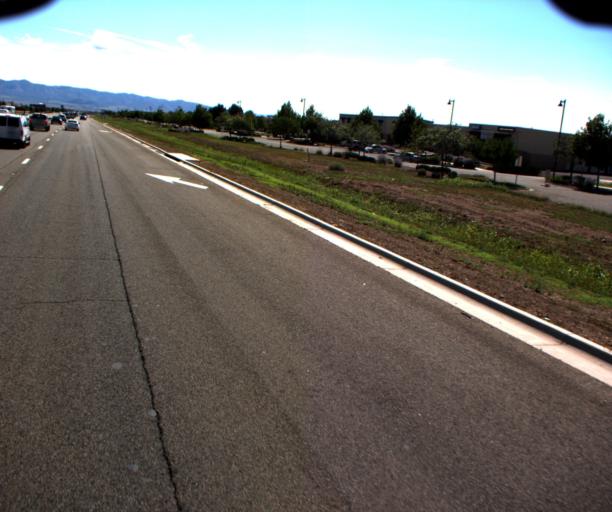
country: US
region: Arizona
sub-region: Yavapai County
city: Prescott Valley
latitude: 34.5808
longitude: -112.3539
